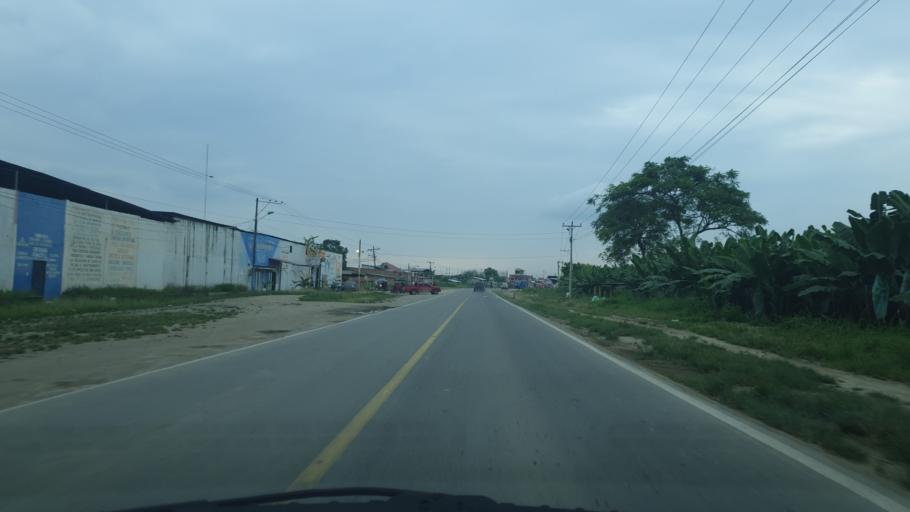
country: EC
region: El Oro
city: Pasaje
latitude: -3.3455
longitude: -79.8139
